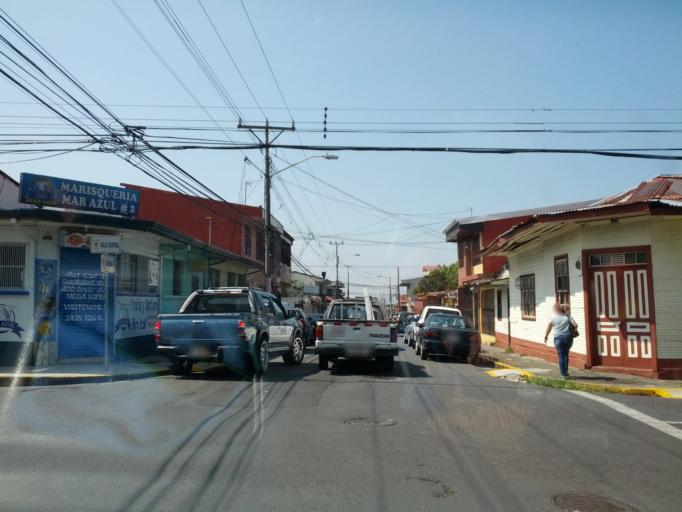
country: CR
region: Alajuela
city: Alajuela
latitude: 10.0196
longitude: -84.2142
